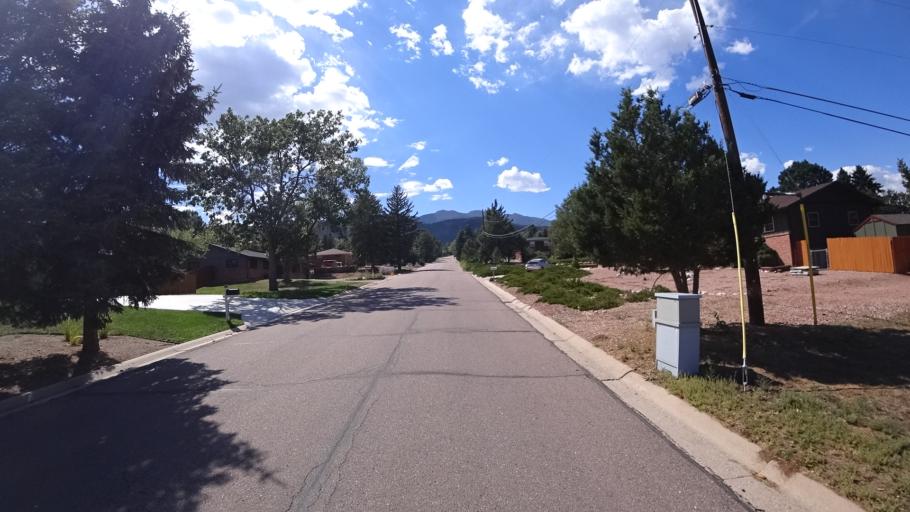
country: US
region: Colorado
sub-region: El Paso County
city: Colorado Springs
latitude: 38.8123
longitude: -104.8615
